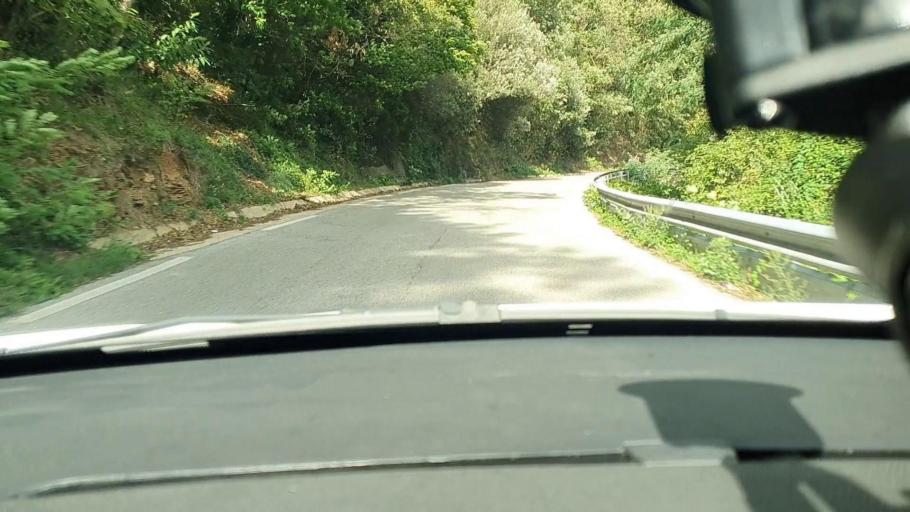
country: FR
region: Languedoc-Roussillon
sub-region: Departement du Gard
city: Laval-Pradel
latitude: 44.2495
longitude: 4.0606
